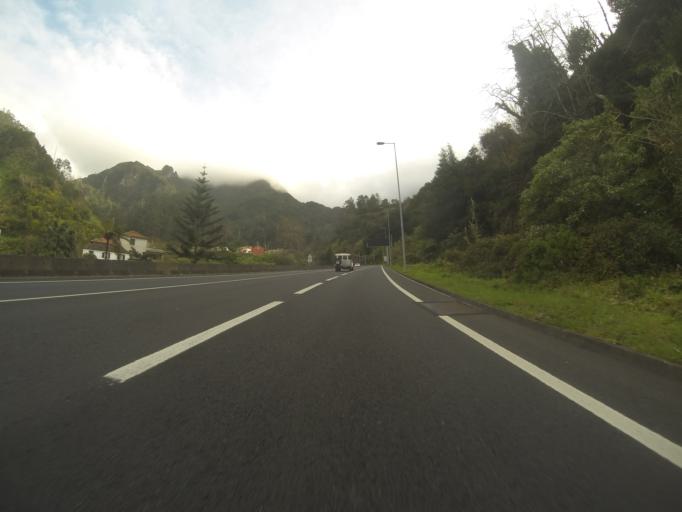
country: PT
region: Madeira
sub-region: Sao Vicente
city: Sao Vicente
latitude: 32.7708
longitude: -17.0300
